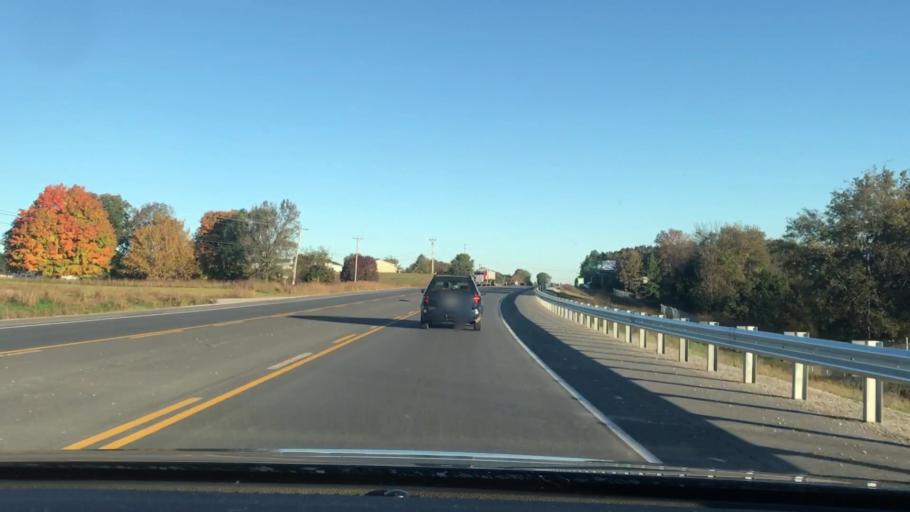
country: US
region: Kentucky
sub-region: Simpson County
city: Franklin
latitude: 36.6808
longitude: -86.5663
